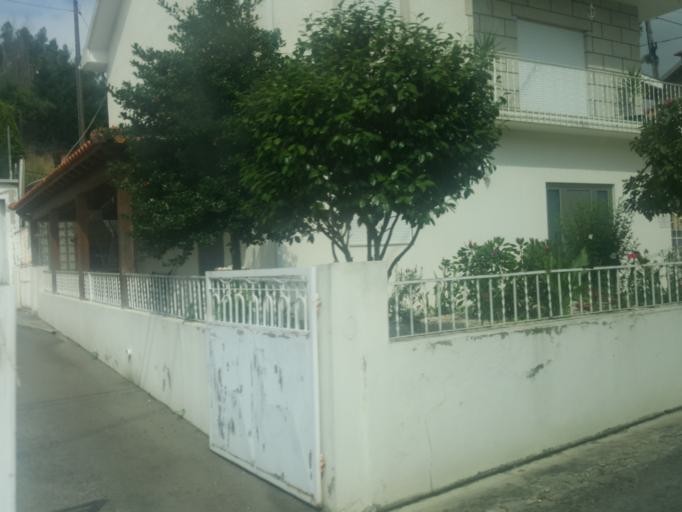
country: PT
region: Porto
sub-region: Marco de Canaveses
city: Marco de Canavezes
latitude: 41.1753
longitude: -8.1916
